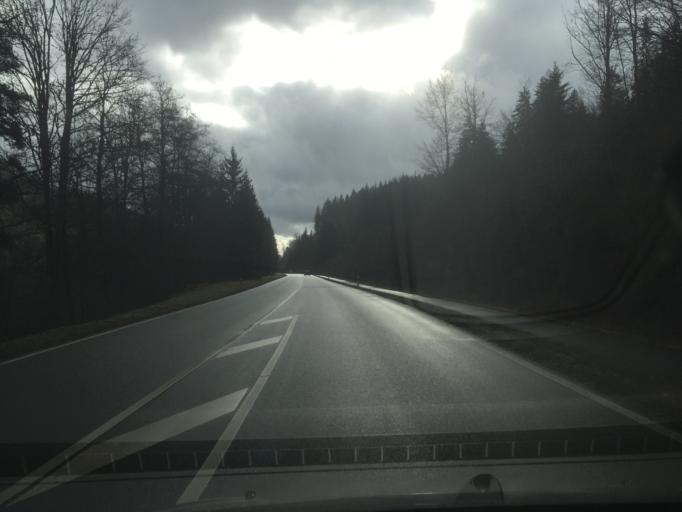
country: DE
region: Baden-Wuerttemberg
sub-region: Freiburg Region
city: Schluchsee
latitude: 47.7861
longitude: 8.1804
